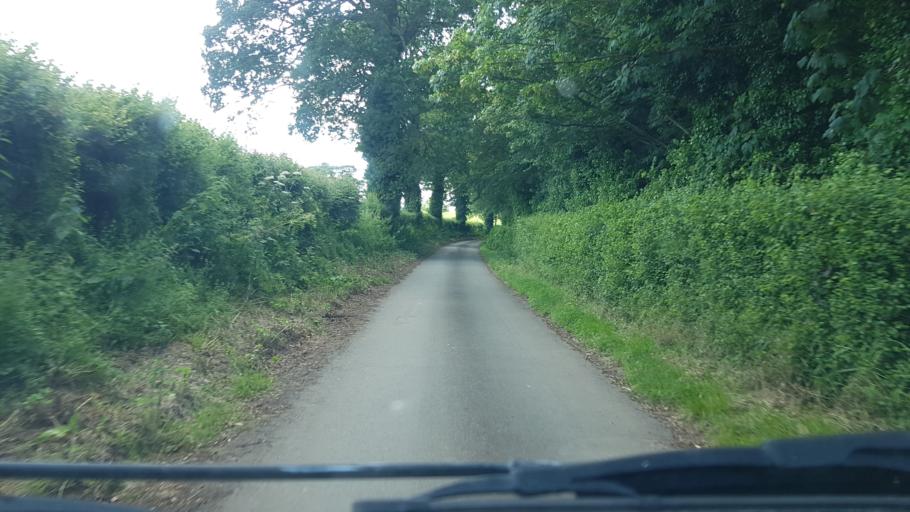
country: GB
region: England
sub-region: Shropshire
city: Romsley
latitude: 52.4569
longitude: -2.2599
